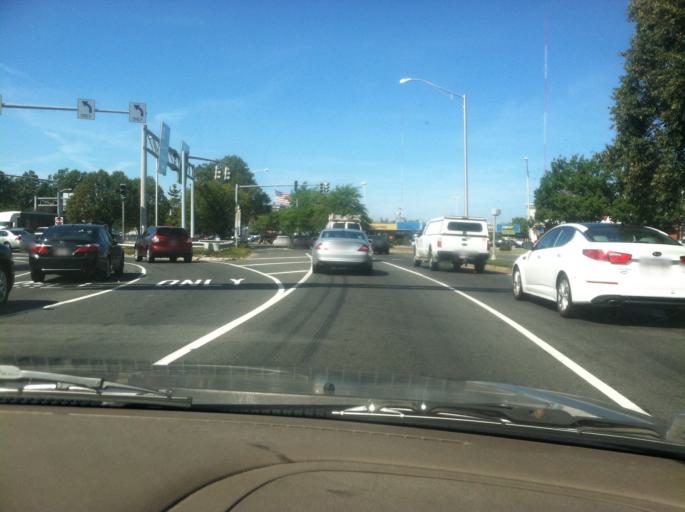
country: US
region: Massachusetts
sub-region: Suffolk County
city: Chelsea
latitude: 42.3878
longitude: -71.0372
